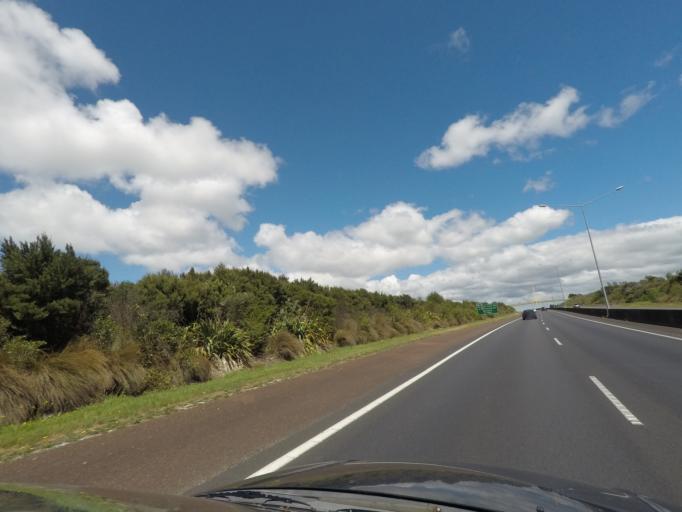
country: NZ
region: Auckland
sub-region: Auckland
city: Rosebank
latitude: -36.7936
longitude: 174.6508
